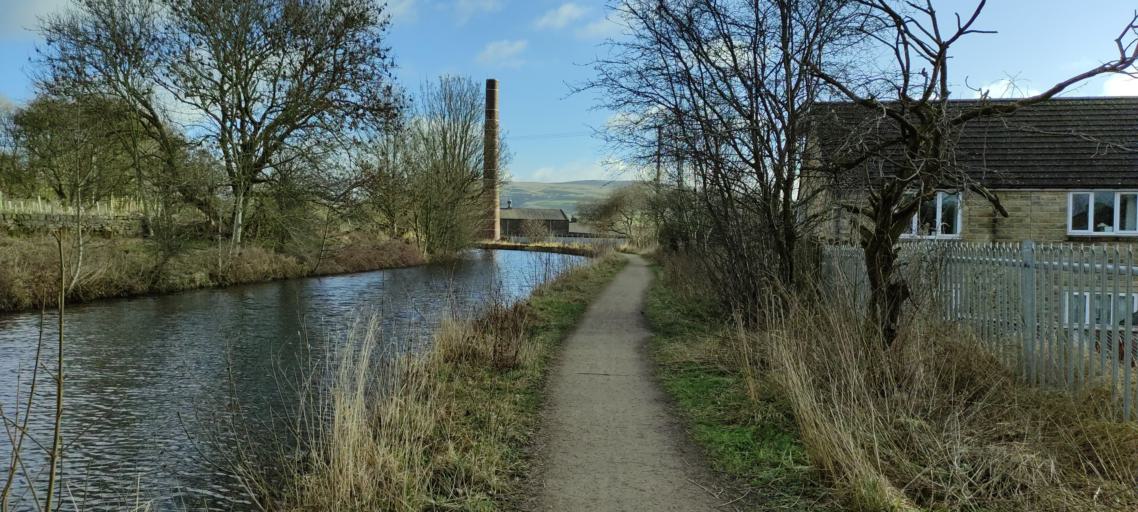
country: GB
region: England
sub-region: North Yorkshire
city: Skipton
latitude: 53.9595
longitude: -2.0384
